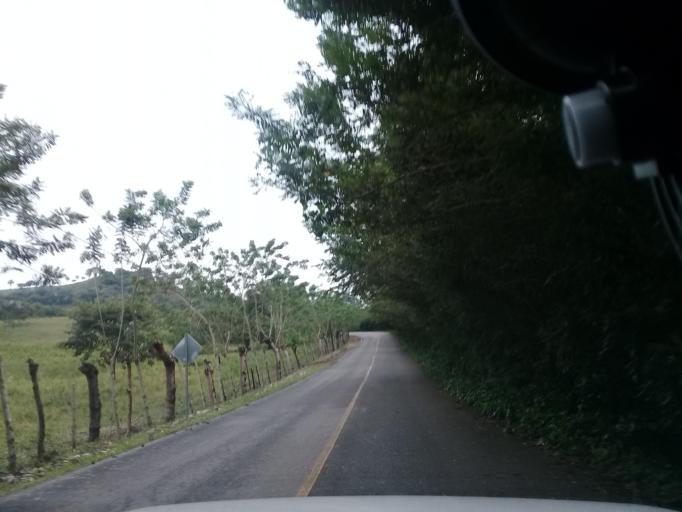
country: MX
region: Veracruz
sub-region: Chalma
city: San Pedro Coyutla
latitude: 21.2167
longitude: -98.4294
